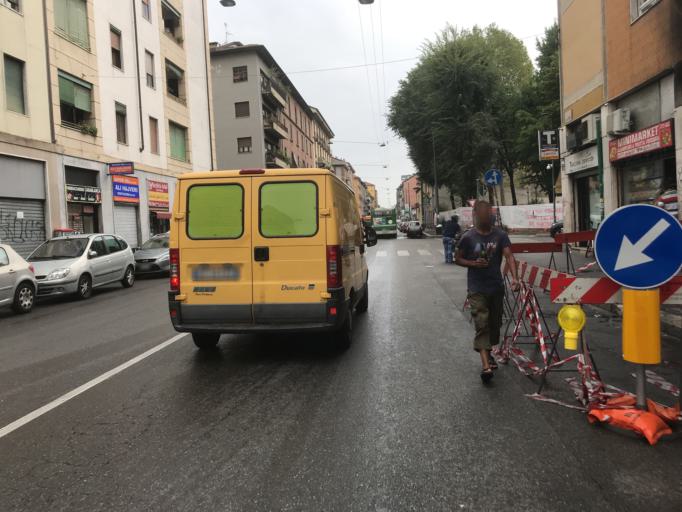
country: IT
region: Lombardy
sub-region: Citta metropolitana di Milano
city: Sesto San Giovanni
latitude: 45.4940
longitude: 9.2270
